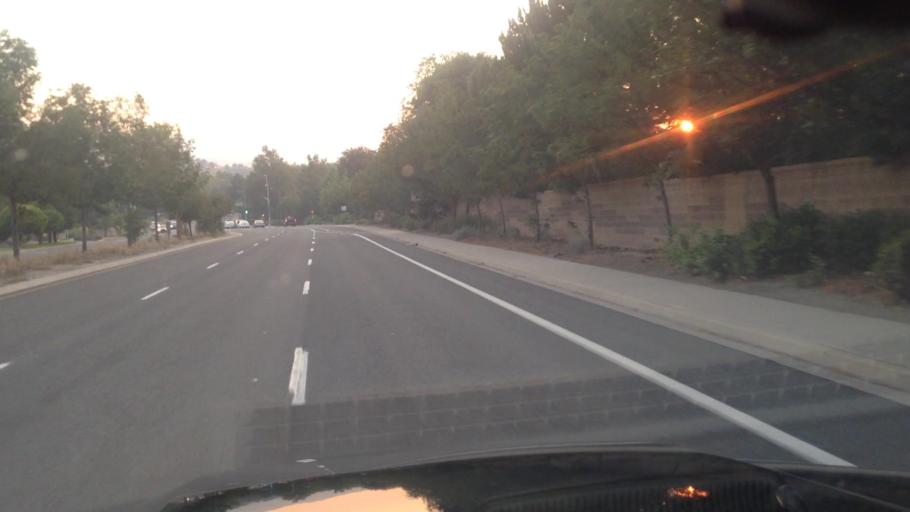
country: US
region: Nevada
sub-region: Washoe County
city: Reno
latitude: 39.4768
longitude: -119.8054
